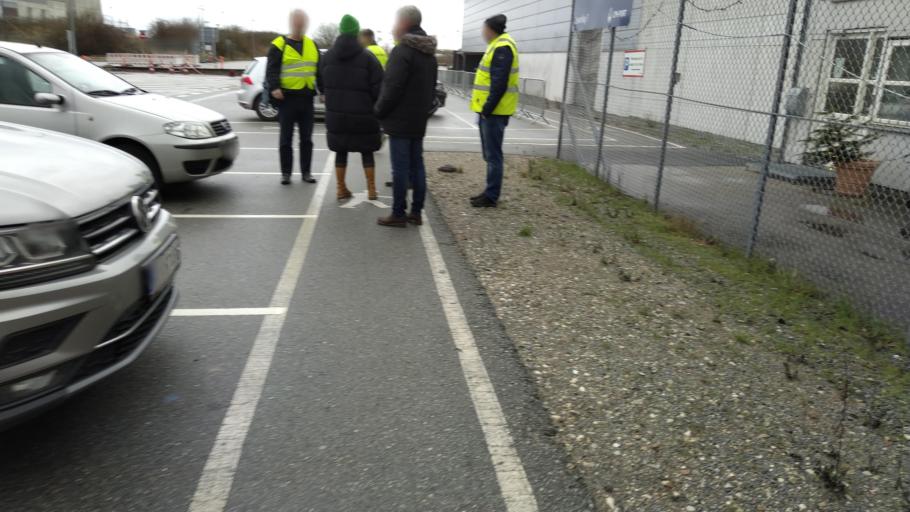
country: DK
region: Capital Region
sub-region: Kobenhavn
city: Christianshavn
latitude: 55.7137
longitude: 12.5951
